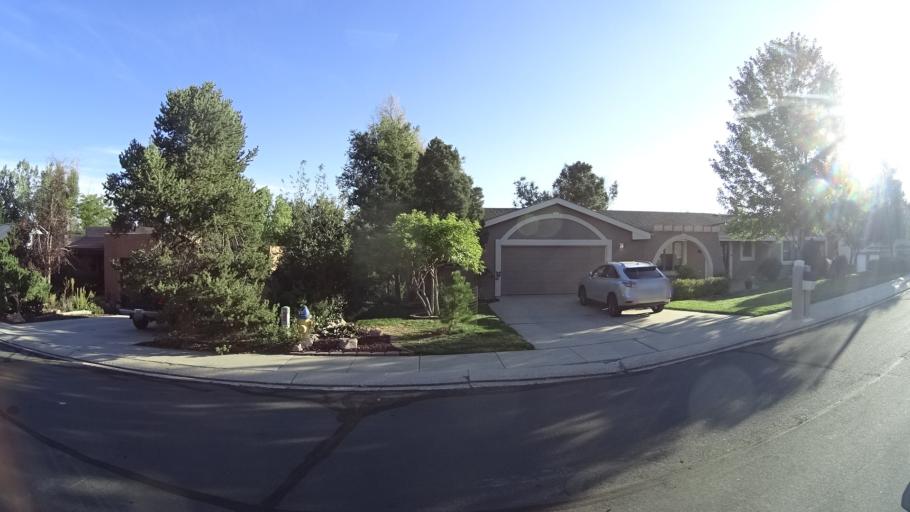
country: US
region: Colorado
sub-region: El Paso County
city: Cimarron Hills
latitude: 38.8887
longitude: -104.7671
